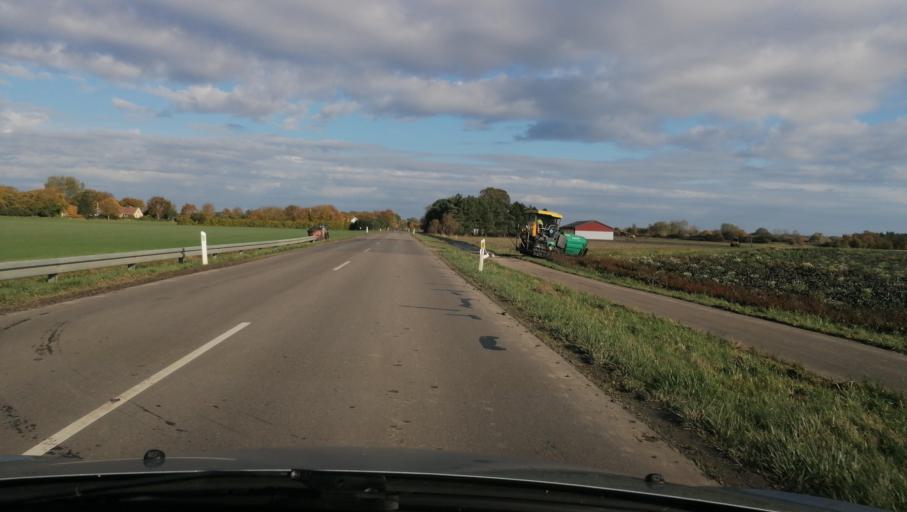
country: DK
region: Zealand
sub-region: Odsherred Kommune
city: Asnaes
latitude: 55.7950
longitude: 11.4635
